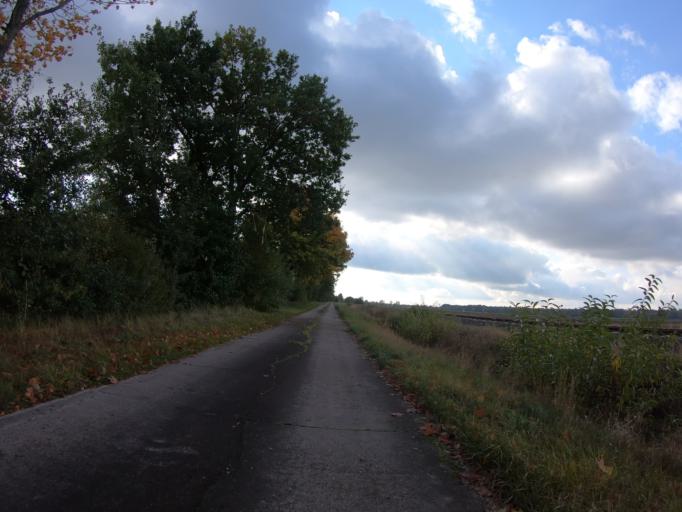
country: DE
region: Lower Saxony
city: Wahrenholz
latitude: 52.5855
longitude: 10.6098
